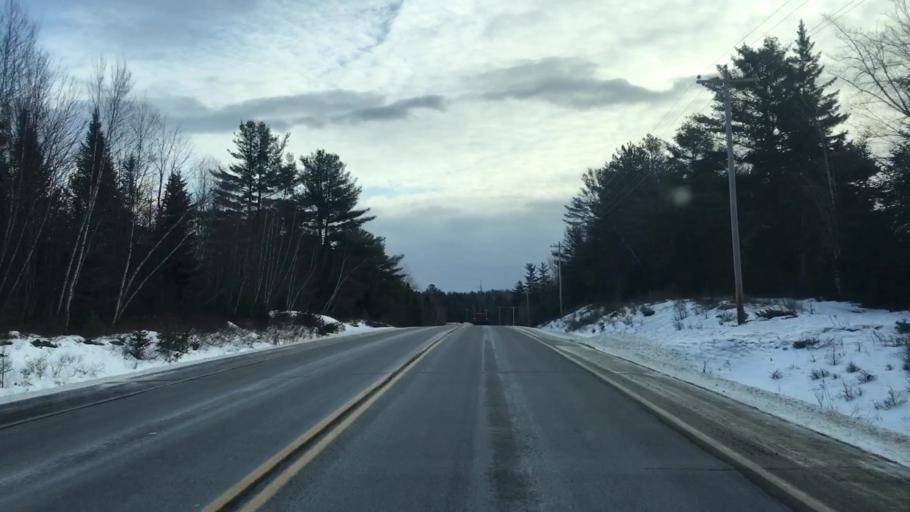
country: US
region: Maine
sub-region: Washington County
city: Machias
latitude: 45.0002
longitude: -67.6113
